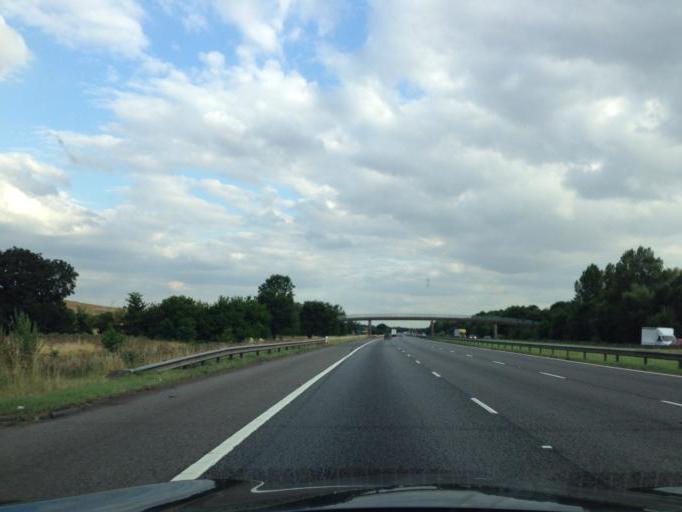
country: GB
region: England
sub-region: Oxfordshire
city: Hanwell
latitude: 52.1104
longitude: -1.3634
